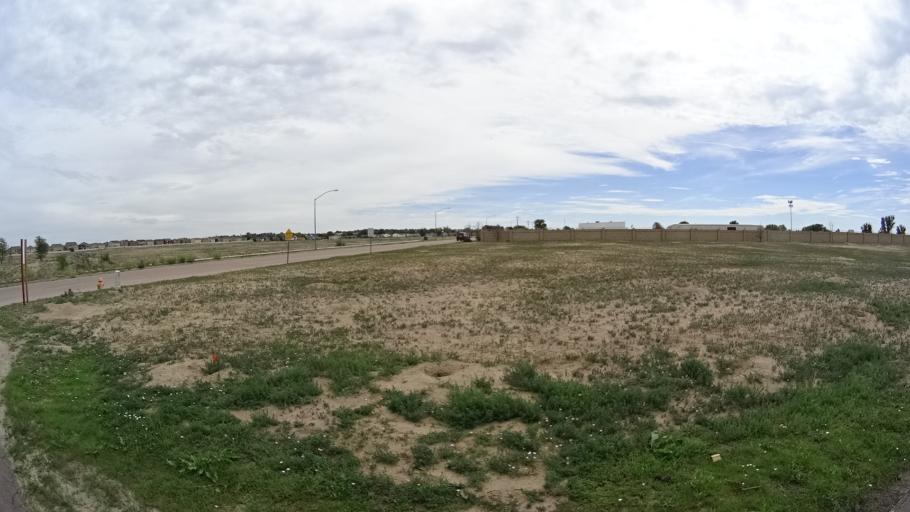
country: US
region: Colorado
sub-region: El Paso County
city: Fountain
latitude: 38.6676
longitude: -104.6938
